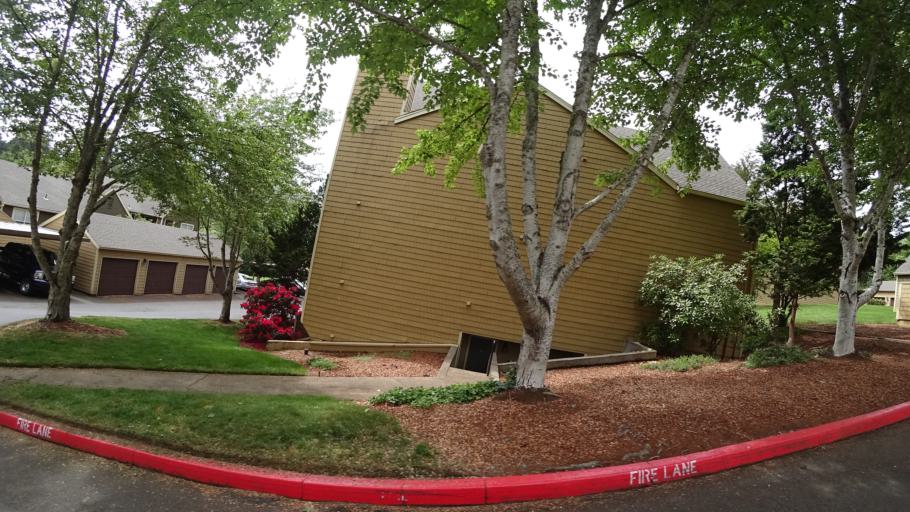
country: US
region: Oregon
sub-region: Washington County
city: Garden Home-Whitford
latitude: 45.4727
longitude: -122.7548
